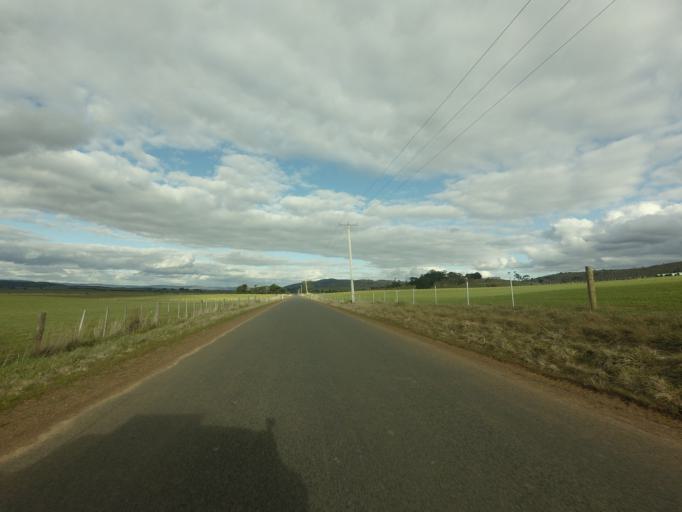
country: AU
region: Tasmania
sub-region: Northern Midlands
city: Evandale
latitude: -41.8937
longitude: 147.3371
